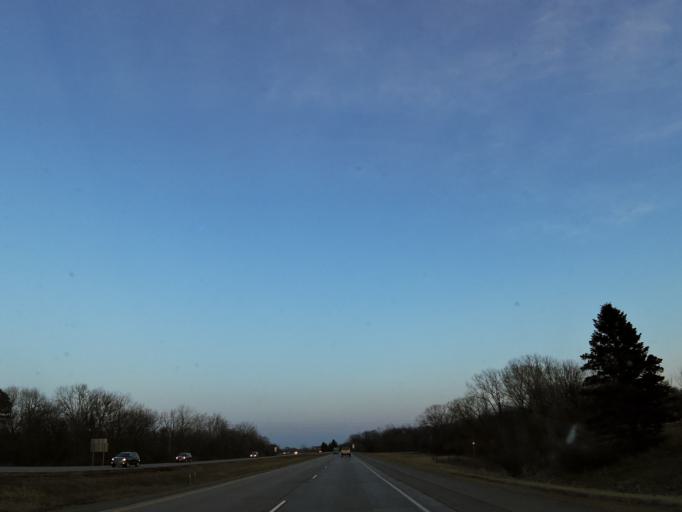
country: US
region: Minnesota
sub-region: Mower County
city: Austin
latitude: 43.6725
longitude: -92.9220
